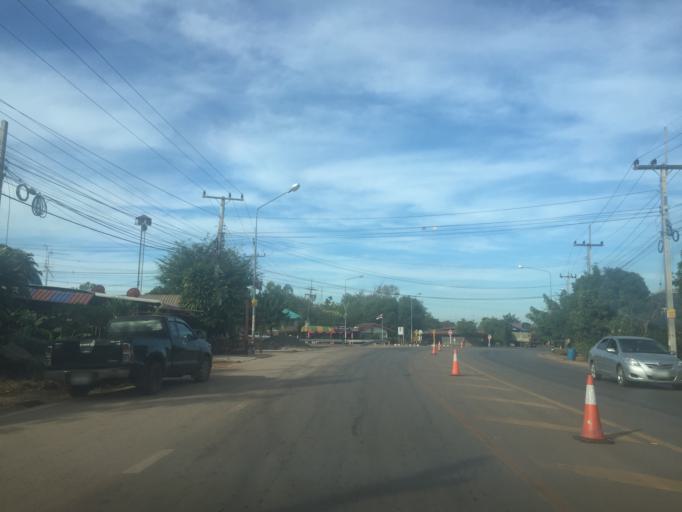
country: TH
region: Changwat Udon Thani
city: Si That
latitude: 16.9875
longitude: 103.1564
